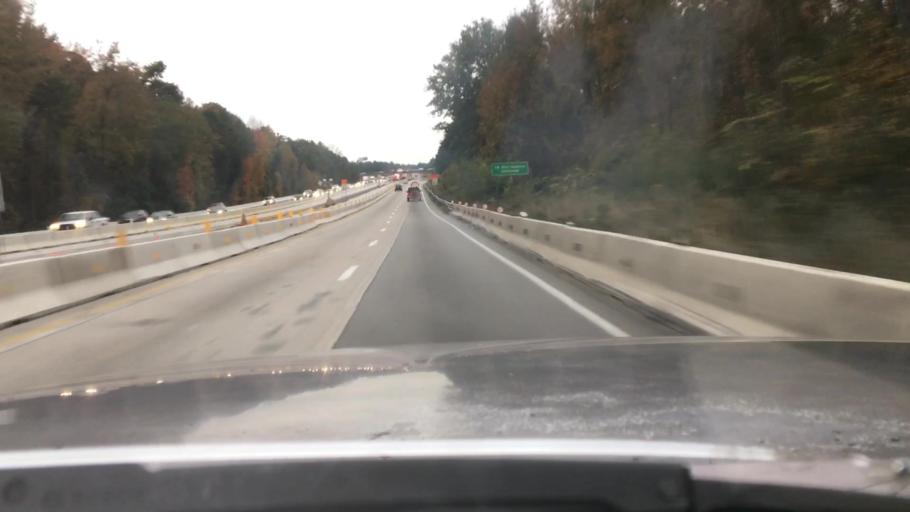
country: US
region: South Carolina
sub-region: Lexington County
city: Lexington
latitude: 33.9850
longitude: -81.1923
